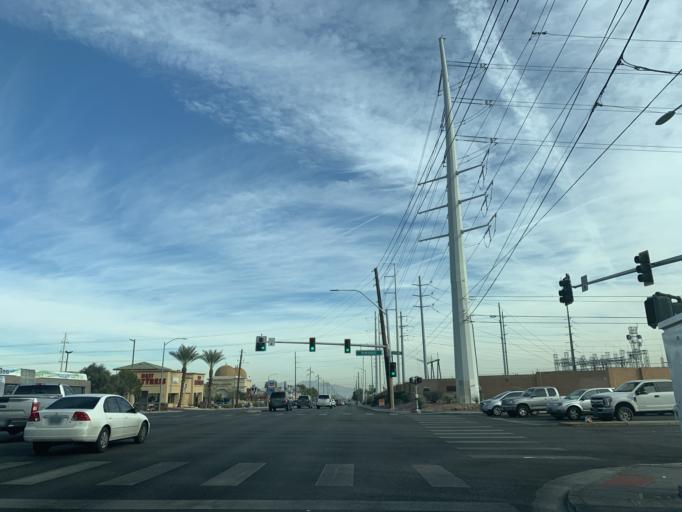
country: US
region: Nevada
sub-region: Clark County
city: Spring Valley
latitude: 36.1590
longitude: -115.2806
